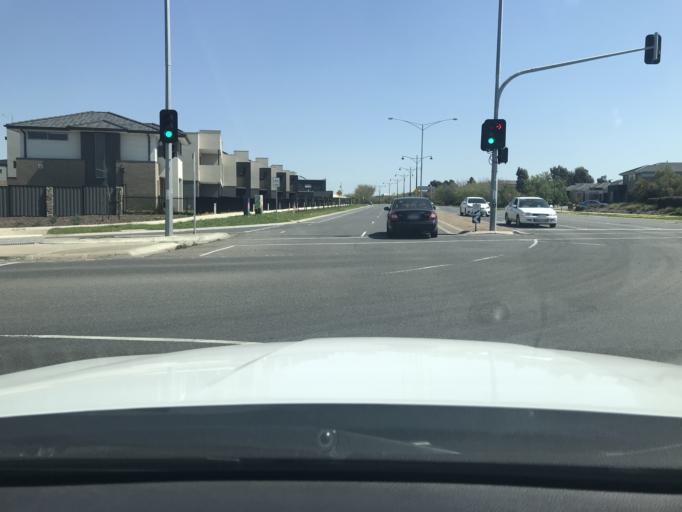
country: AU
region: Victoria
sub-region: Hume
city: Craigieburn
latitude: -37.5861
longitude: 144.9114
